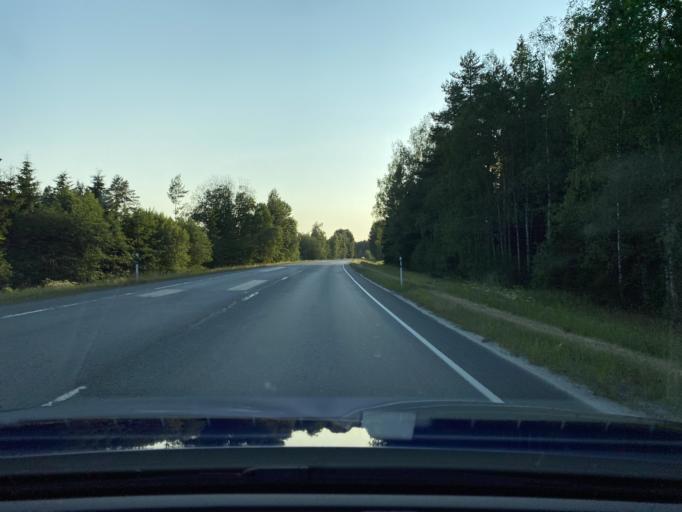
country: FI
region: Haeme
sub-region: Forssa
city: Tammela
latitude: 60.8266
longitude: 23.7435
